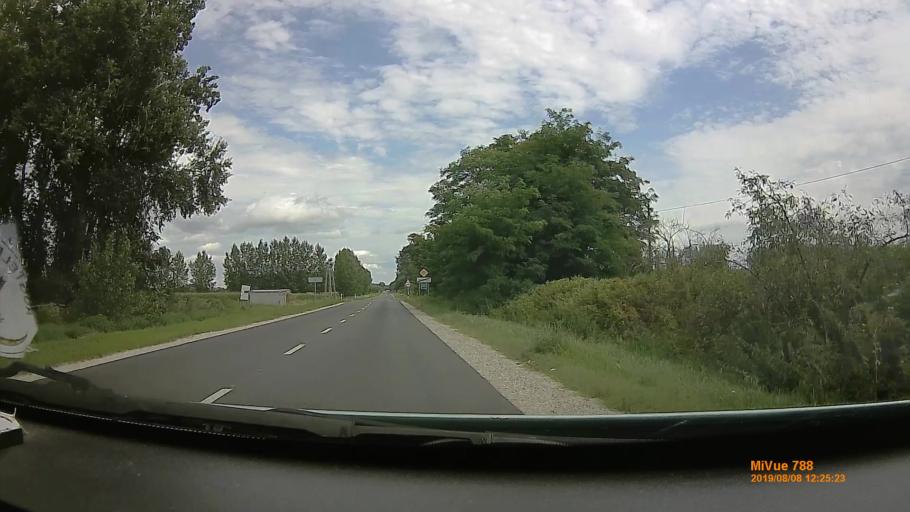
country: HU
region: Szabolcs-Szatmar-Bereg
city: Nyirbogat
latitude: 47.8105
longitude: 22.0702
